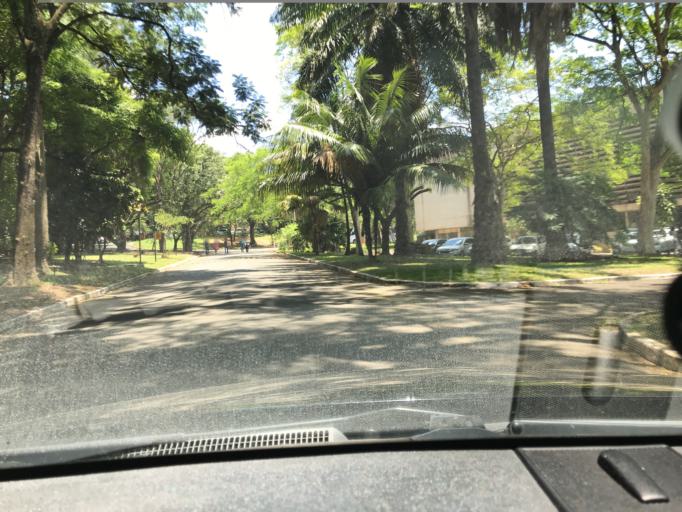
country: BR
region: Sao Paulo
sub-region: Campinas
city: Campinas
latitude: -22.8768
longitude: -47.0743
